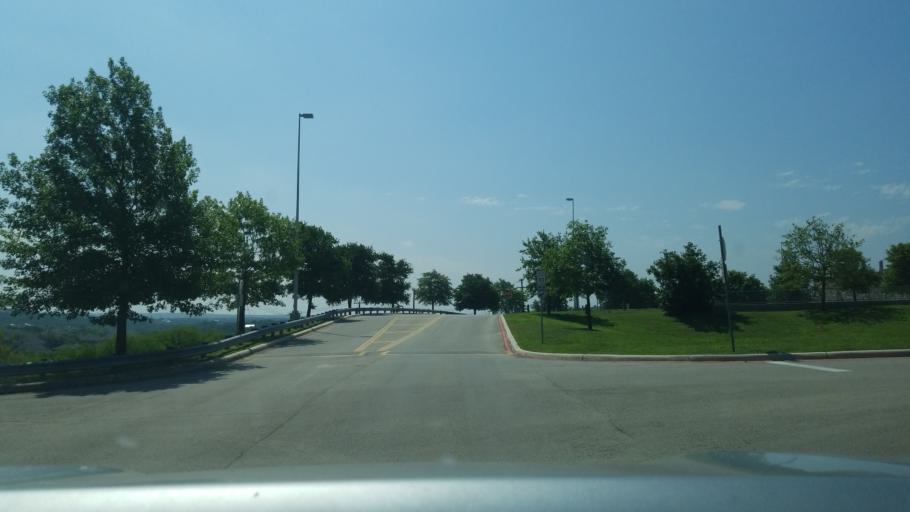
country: US
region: Texas
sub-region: Bexar County
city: Timberwood Park
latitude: 29.6585
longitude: -98.4341
